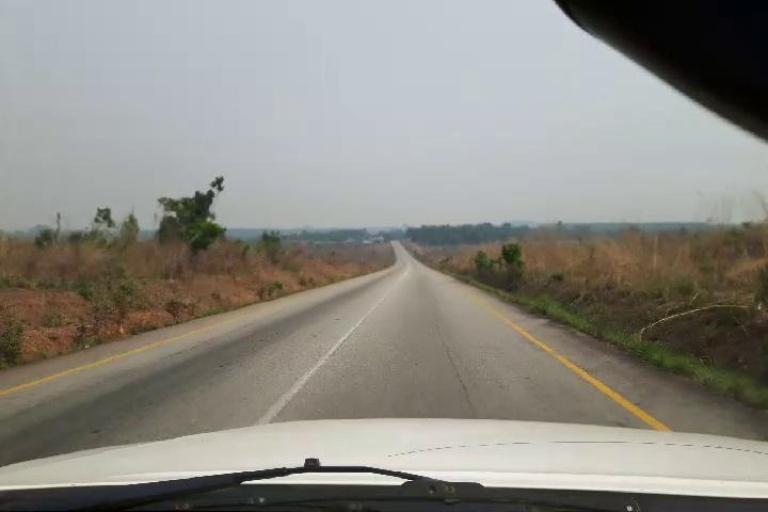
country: SL
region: Southern Province
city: Largo
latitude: 8.2262
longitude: -12.0766
